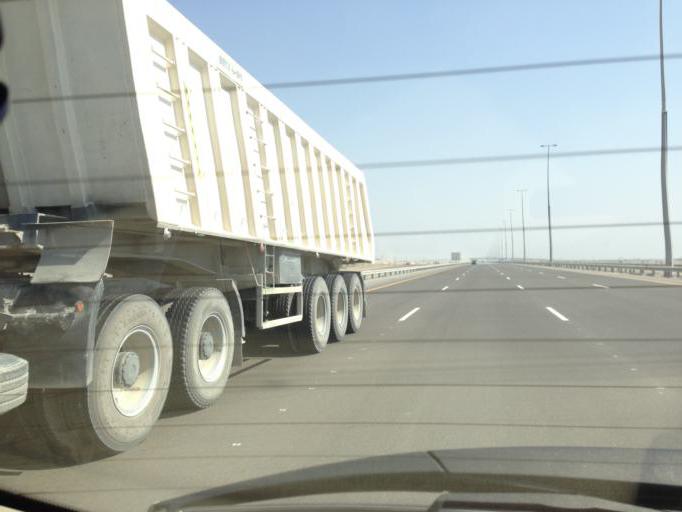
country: OM
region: Al Batinah
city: Barka'
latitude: 23.6124
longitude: 57.8310
